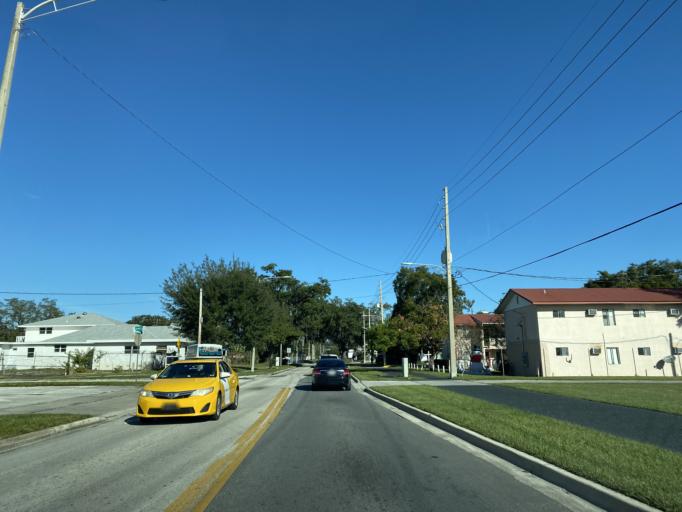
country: US
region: Florida
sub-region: Orange County
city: Orlando
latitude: 28.5499
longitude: -81.3933
